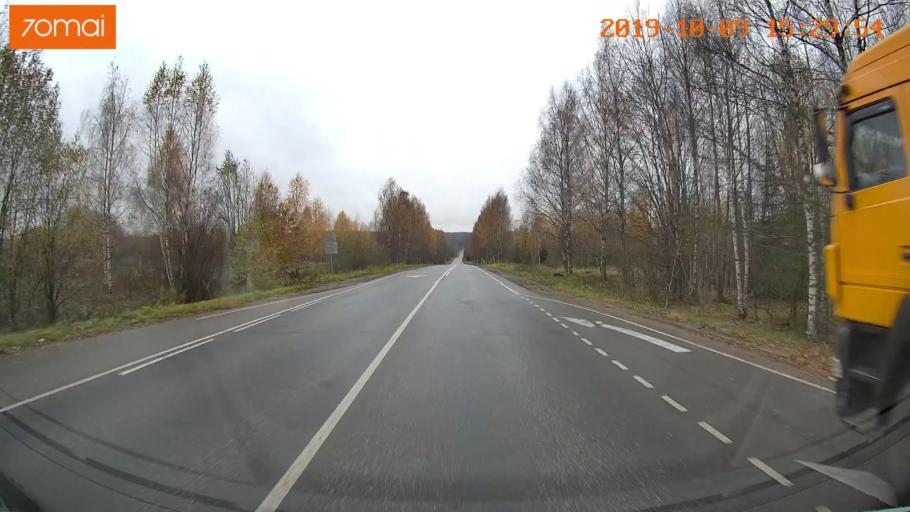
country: RU
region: Kostroma
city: Susanino
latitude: 57.9862
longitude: 41.3352
